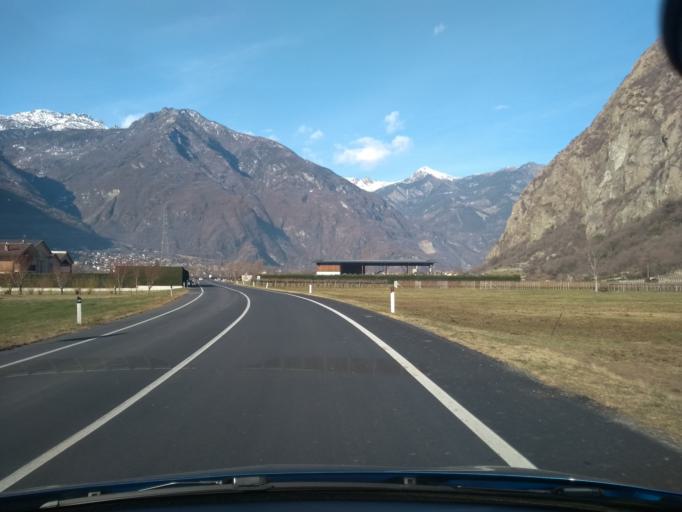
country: IT
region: Aosta Valley
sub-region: Valle d'Aosta
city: Arnad
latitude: 45.6526
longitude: 7.7074
